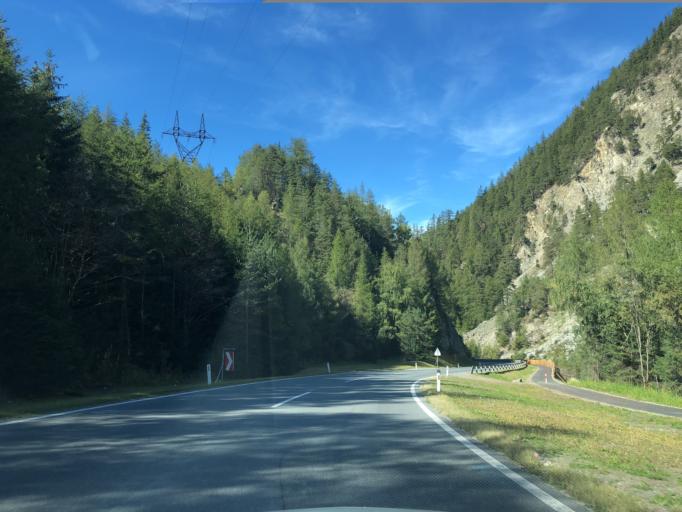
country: AT
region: Tyrol
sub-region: Politischer Bezirk Imst
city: Umhausen
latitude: 47.1131
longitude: 10.9397
